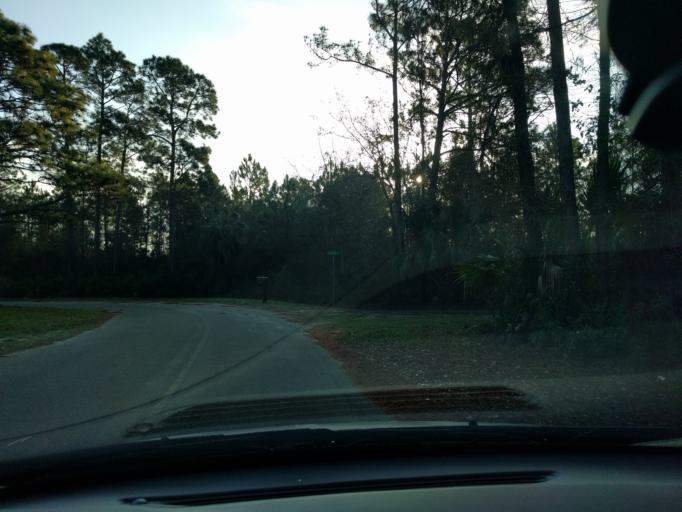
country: US
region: Florida
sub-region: Franklin County
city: Apalachicola
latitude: 29.7167
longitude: -85.0263
